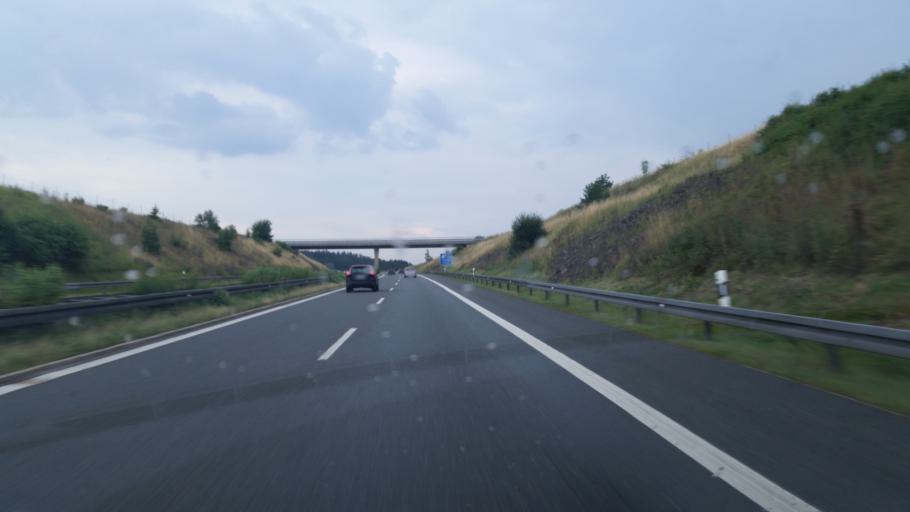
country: DE
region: Bavaria
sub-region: Upper Franconia
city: Trogen
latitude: 50.3633
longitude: 11.9721
